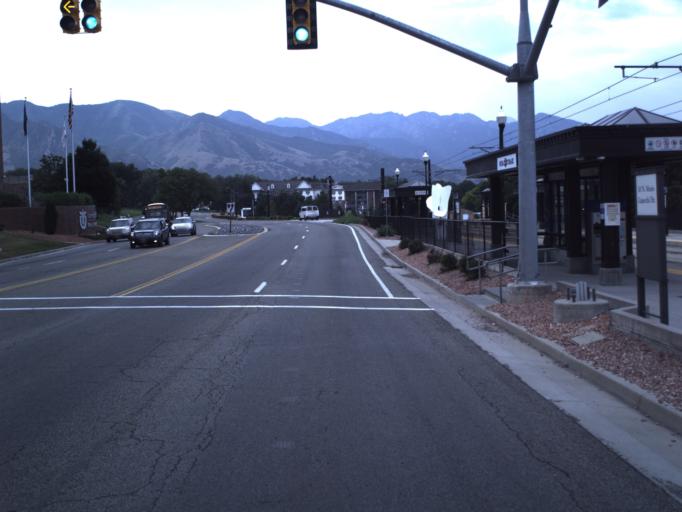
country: US
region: Utah
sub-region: Salt Lake County
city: Salt Lake City
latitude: 40.7700
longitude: -111.8391
